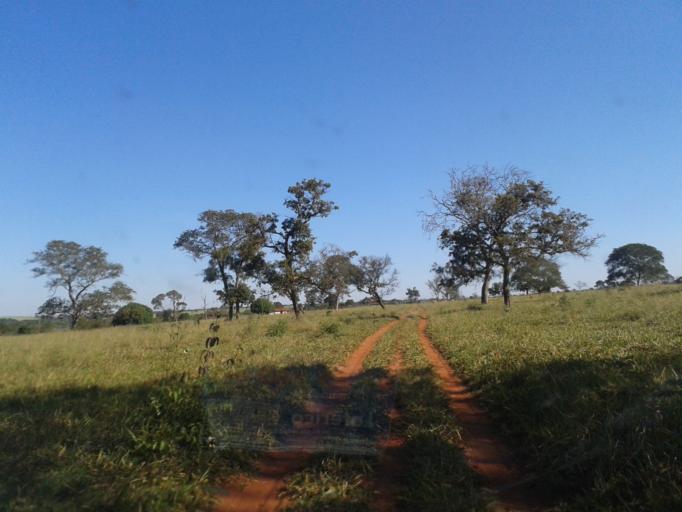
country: BR
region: Minas Gerais
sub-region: Santa Vitoria
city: Santa Vitoria
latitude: -19.0399
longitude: -50.3809
